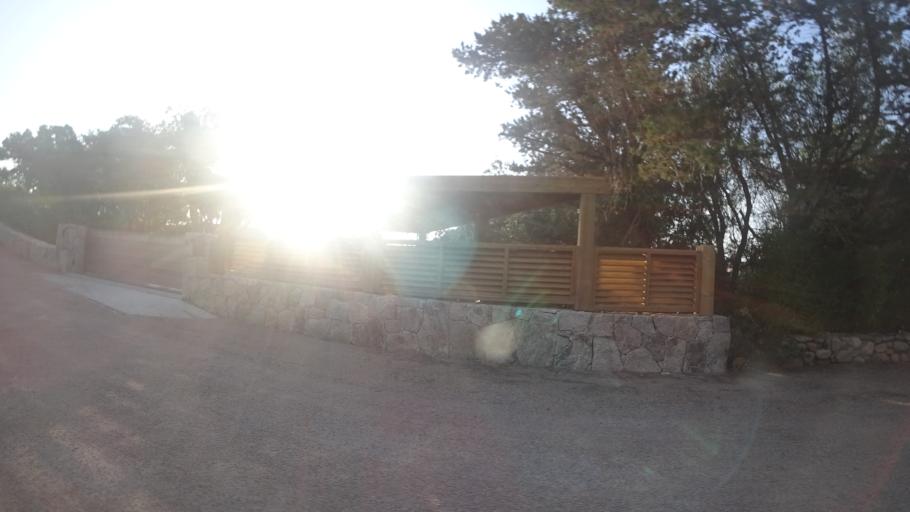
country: FR
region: Corsica
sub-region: Departement de la Corse-du-Sud
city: Porto-Vecchio
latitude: 41.6226
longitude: 9.3527
